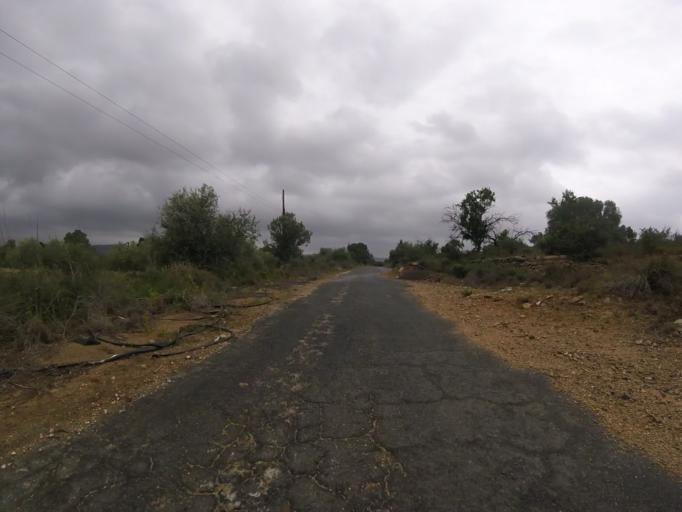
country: ES
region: Valencia
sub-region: Provincia de Castello
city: Alcala de Xivert
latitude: 40.2807
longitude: 0.2253
